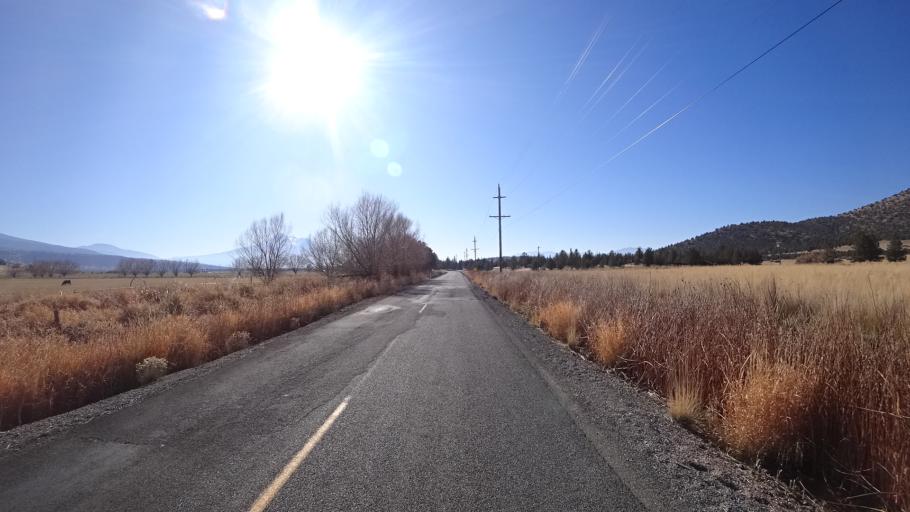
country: US
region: California
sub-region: Siskiyou County
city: Montague
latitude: 41.6762
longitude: -122.3698
